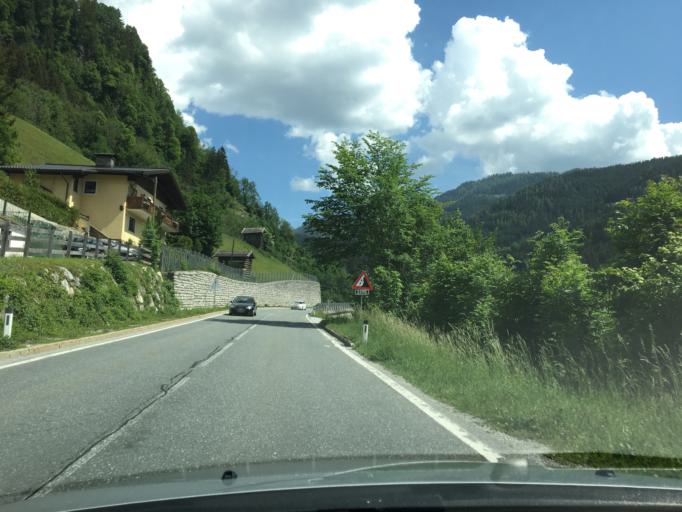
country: AT
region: Salzburg
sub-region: Politischer Bezirk Sankt Johann im Pongau
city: Sankt Johann im Pongau
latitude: 47.3375
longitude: 13.2145
